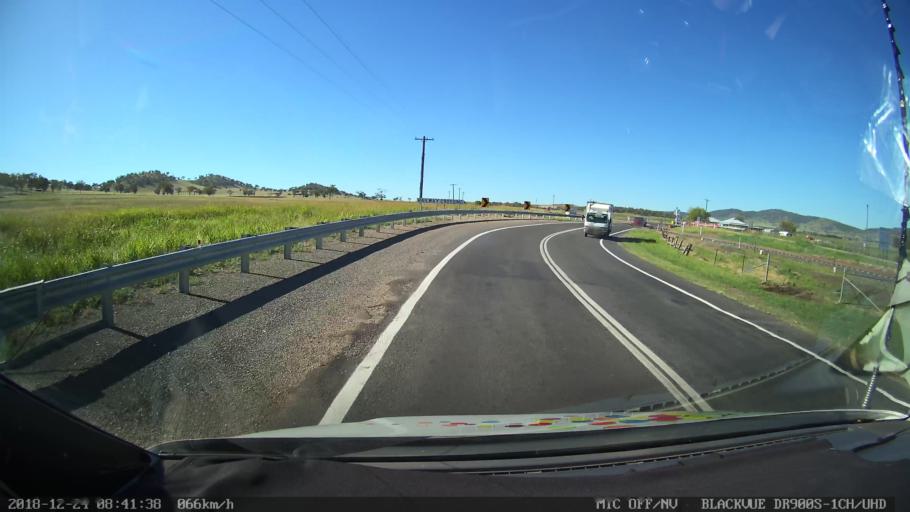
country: AU
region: New South Wales
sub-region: Liverpool Plains
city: Quirindi
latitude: -31.3652
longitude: 150.6450
